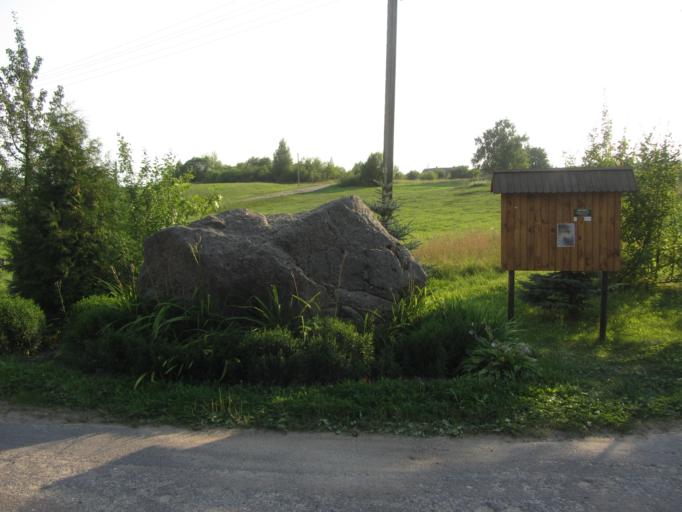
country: LT
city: Lazdijai
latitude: 54.1565
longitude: 23.5375
